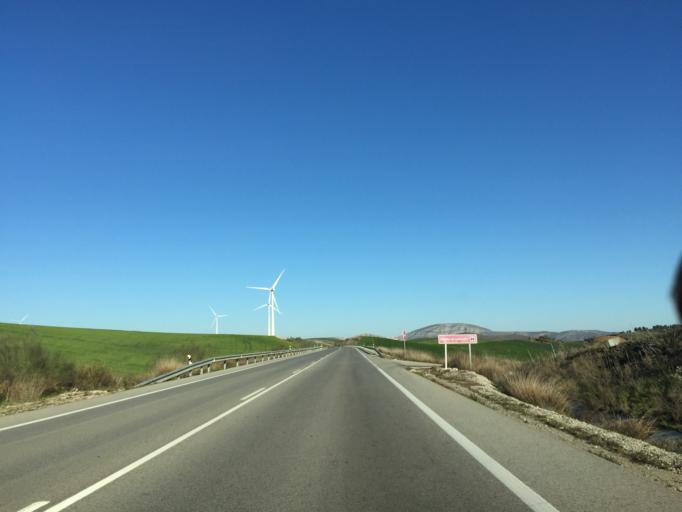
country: ES
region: Andalusia
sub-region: Provincia de Malaga
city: Ardales
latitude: 36.9287
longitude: -4.8536
